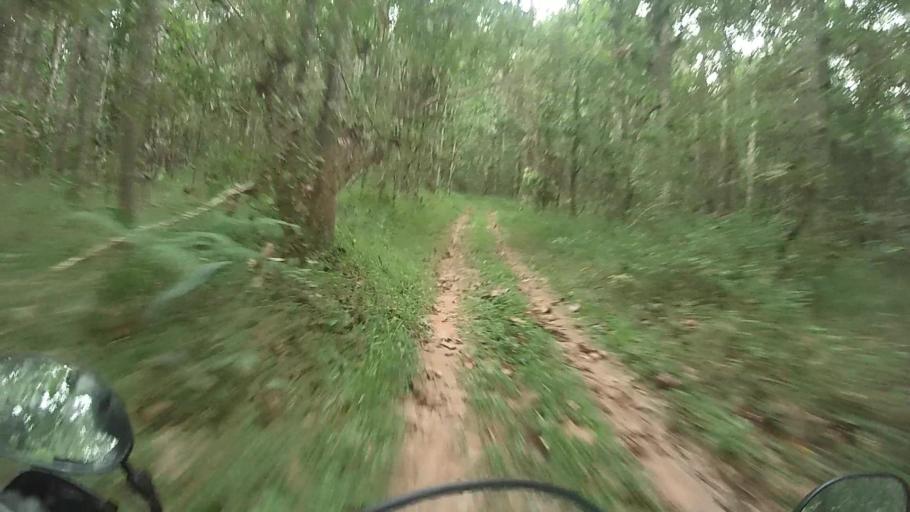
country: TH
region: Chiang Mai
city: Mae On
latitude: 18.8885
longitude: 99.2070
